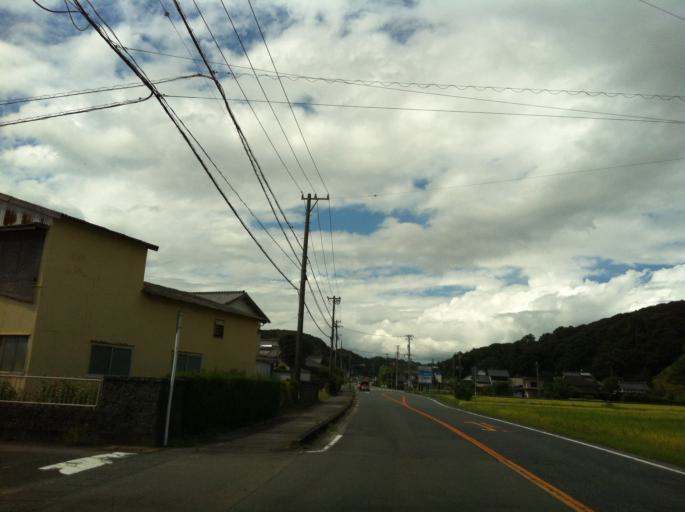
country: JP
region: Shizuoka
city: Kakegawa
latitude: 34.7230
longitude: 138.0493
